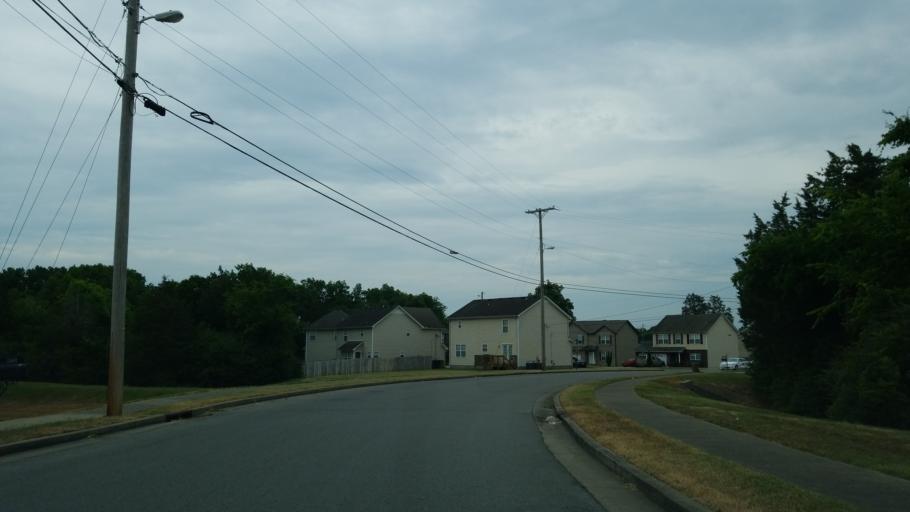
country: US
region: Tennessee
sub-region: Rutherford County
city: La Vergne
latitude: 36.0530
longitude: -86.5957
